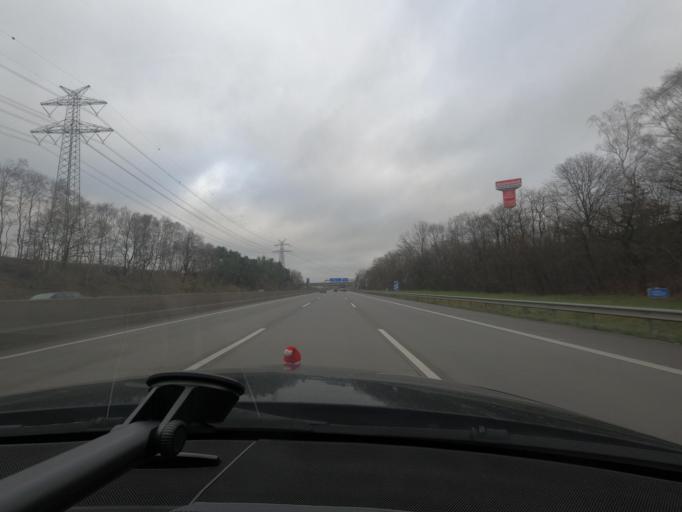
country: DE
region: Schleswig-Holstein
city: Nutzen
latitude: 53.8450
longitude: 9.9330
